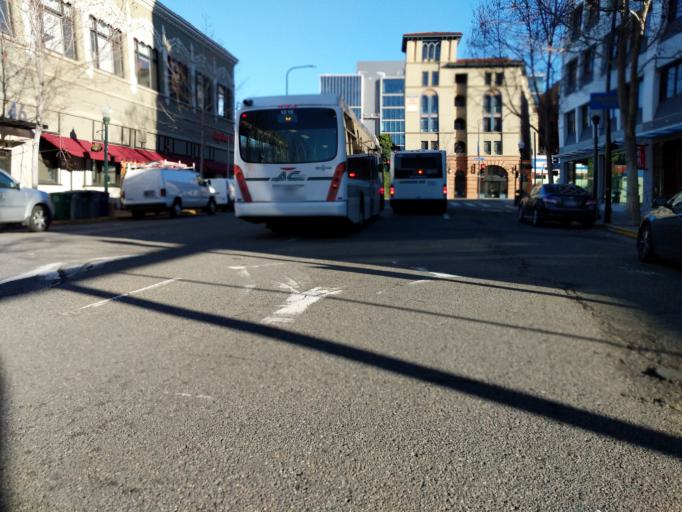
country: US
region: California
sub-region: Alameda County
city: Berkeley
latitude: 37.8717
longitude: -122.2677
